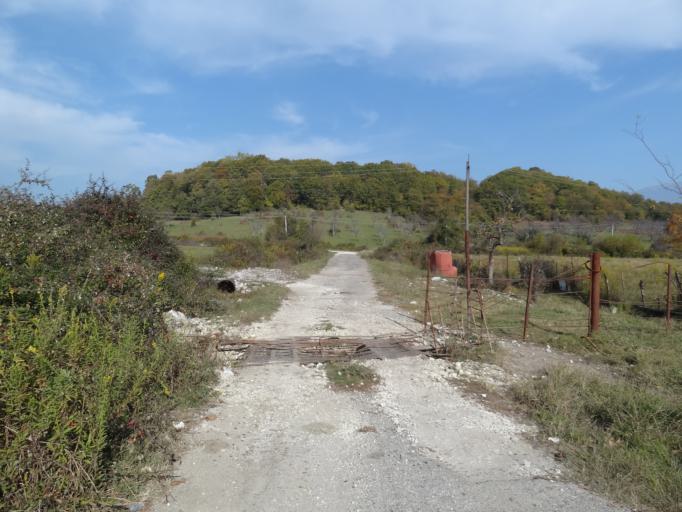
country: GE
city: Gantiadi
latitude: 43.3905
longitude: 40.0345
